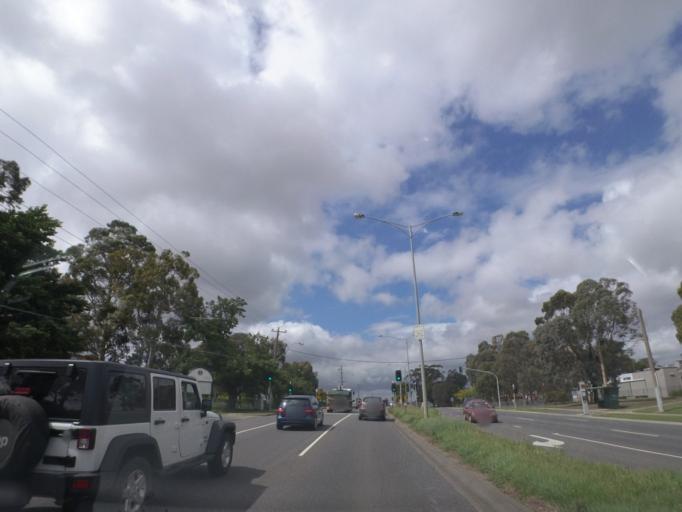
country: AU
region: Victoria
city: Plenty
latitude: -37.6834
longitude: 145.1192
